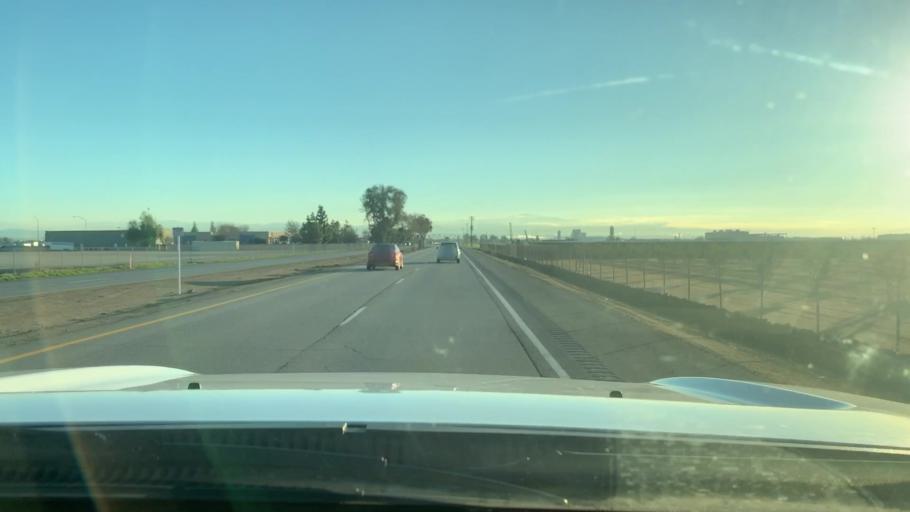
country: US
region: California
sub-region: Kern County
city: Shafter
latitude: 35.4996
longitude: -119.1857
